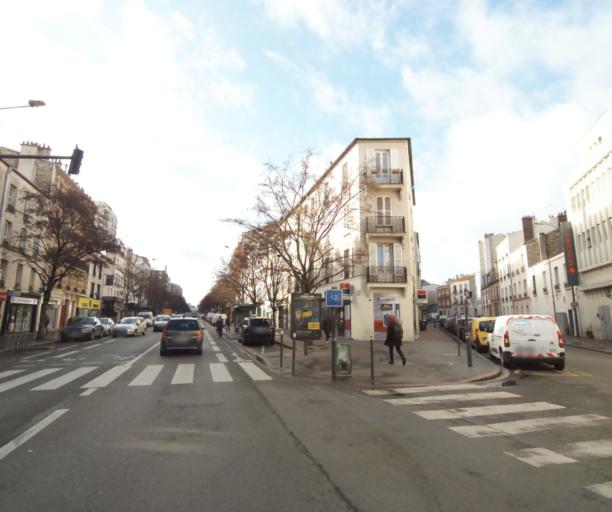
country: FR
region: Ile-de-France
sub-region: Paris
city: Saint-Ouen
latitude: 48.9058
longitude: 2.3317
